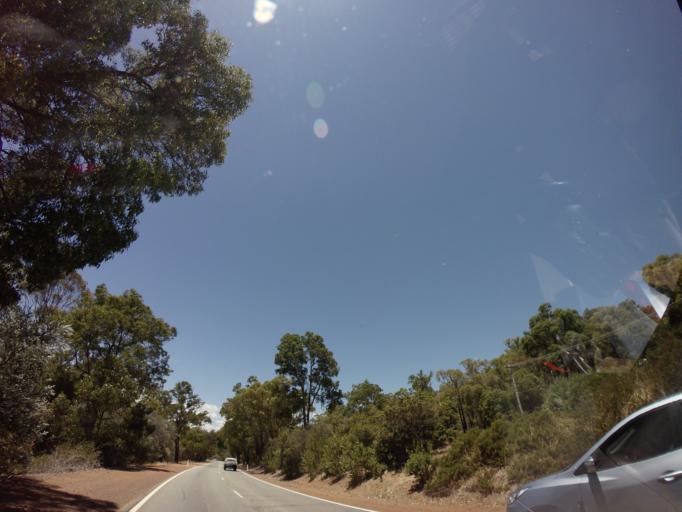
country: AU
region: Western Australia
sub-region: Mundaring
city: Darlington
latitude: -31.9012
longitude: 116.1100
